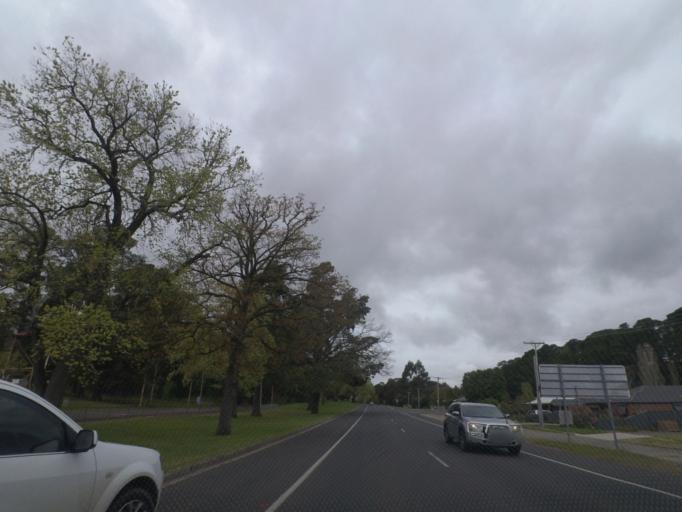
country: AU
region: Victoria
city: Brown Hill
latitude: -37.4190
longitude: 143.8963
